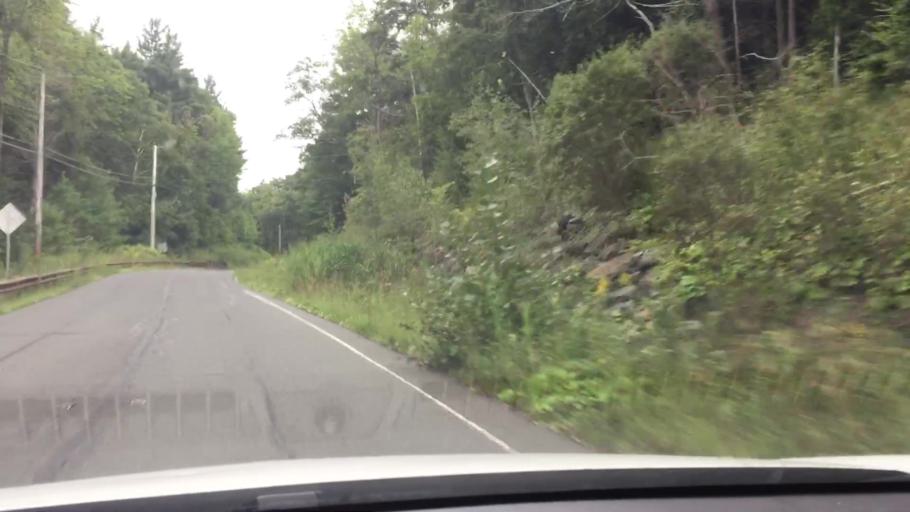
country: US
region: Massachusetts
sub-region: Berkshire County
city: Becket
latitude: 42.2640
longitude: -73.0016
